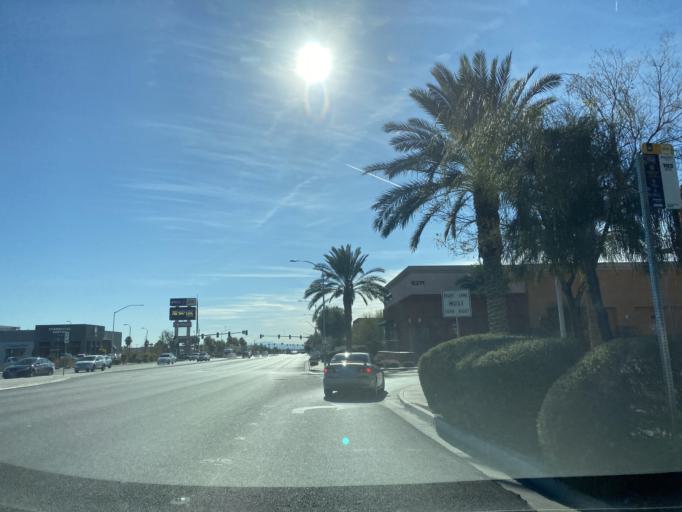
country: US
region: Nevada
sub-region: Clark County
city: North Las Vegas
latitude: 36.2723
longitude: -115.2069
